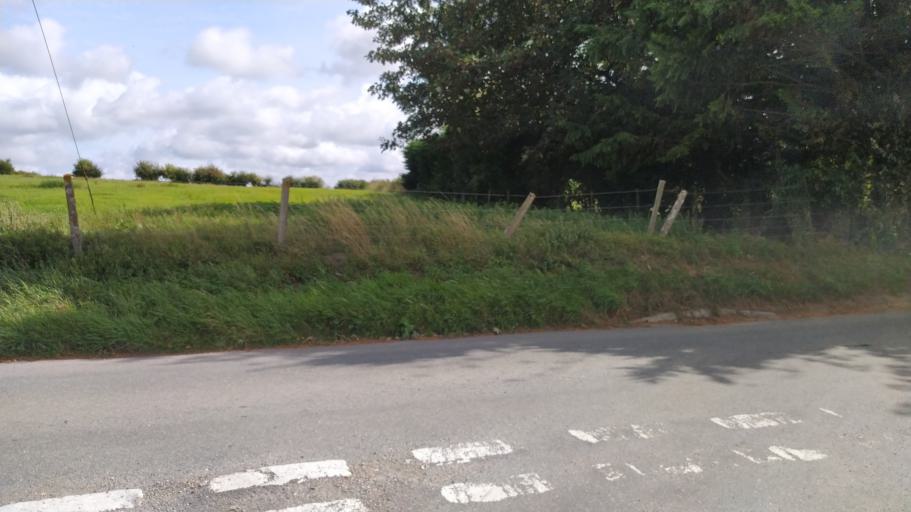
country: GB
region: England
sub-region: Dorset
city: Blandford Forum
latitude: 50.8239
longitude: -2.1105
